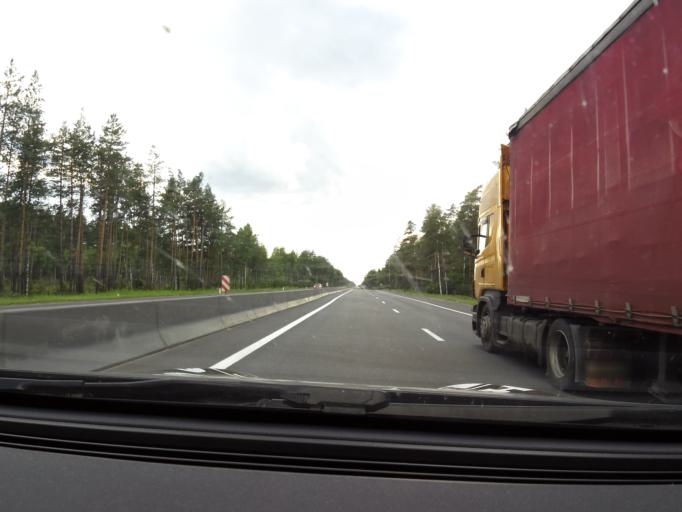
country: RU
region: Nizjnij Novgorod
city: Yuganets
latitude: 56.2891
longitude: 43.2565
